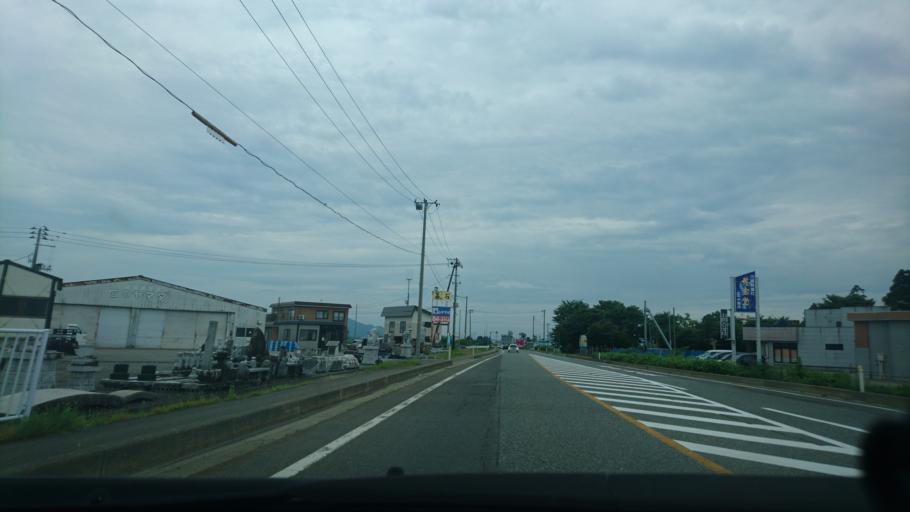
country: JP
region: Akita
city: Omagari
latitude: 39.4181
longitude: 140.5412
